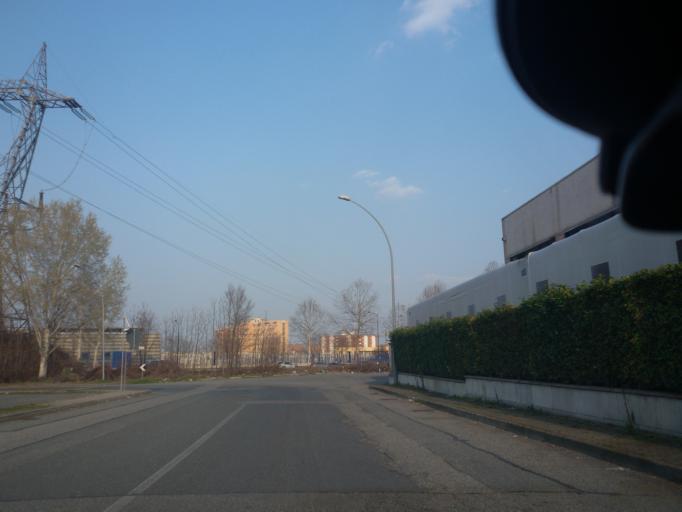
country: IT
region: Piedmont
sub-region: Provincia di Torino
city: Savonera
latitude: 45.1008
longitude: 7.6130
